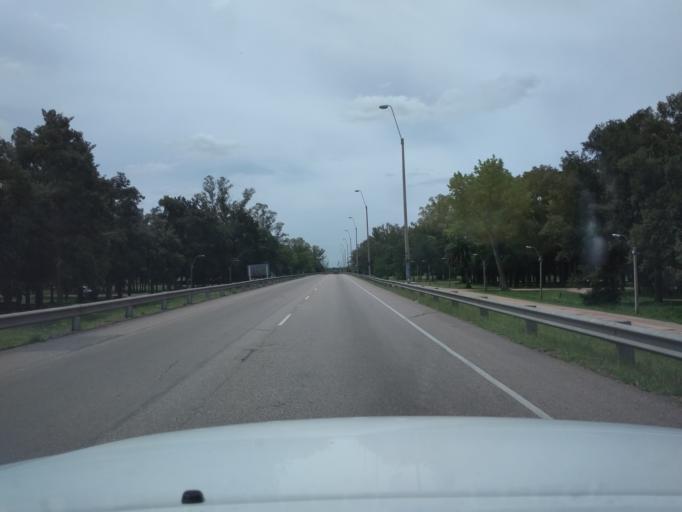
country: UY
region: Canelones
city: Canelones
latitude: -34.5286
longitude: -56.2712
